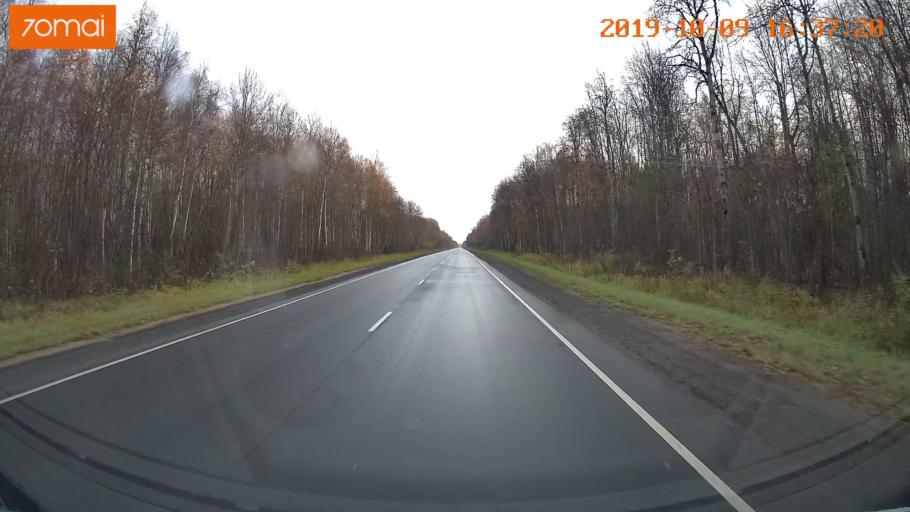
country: RU
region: Kostroma
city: Volgorechensk
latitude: 57.5285
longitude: 41.0233
